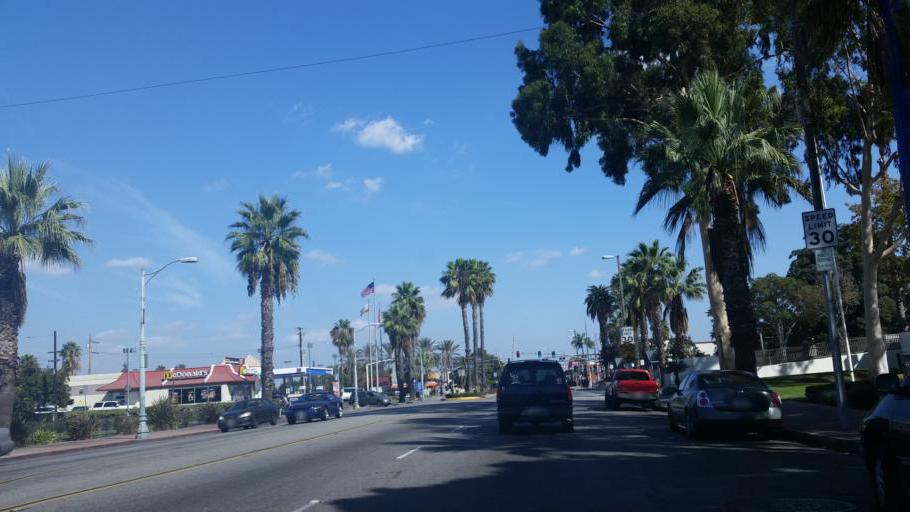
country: US
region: California
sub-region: Los Angeles County
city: Compton
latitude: 33.8959
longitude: -118.2261
